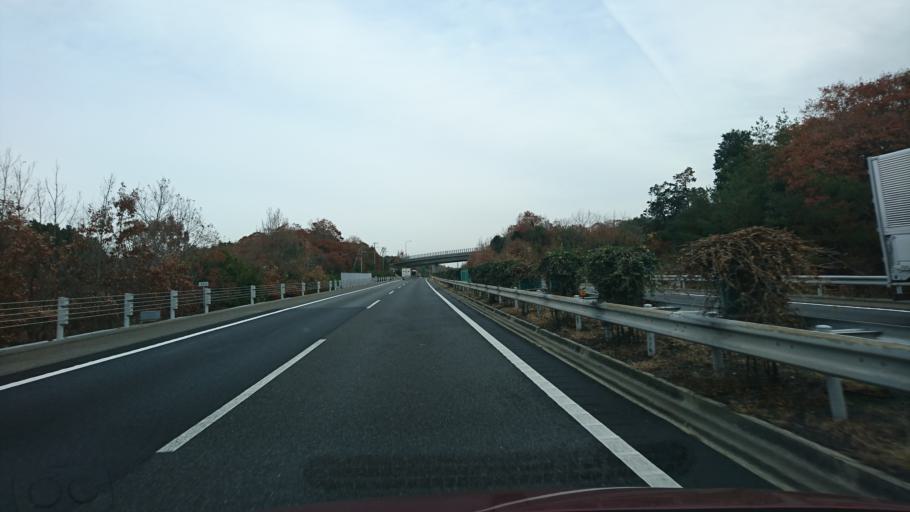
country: JP
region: Hyogo
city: Miki
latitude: 34.8101
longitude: 135.0738
